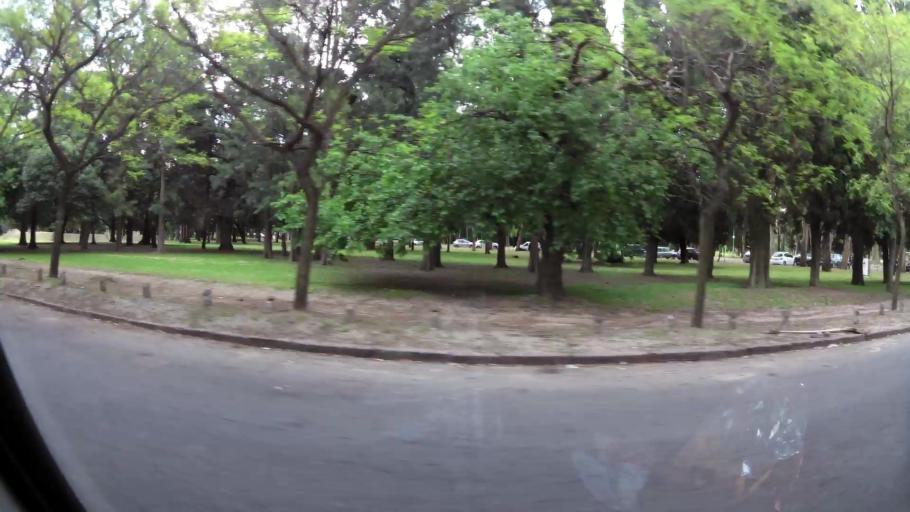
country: AR
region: Buenos Aires
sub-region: Partido de La Plata
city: La Plata
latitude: -34.9102
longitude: -57.9300
